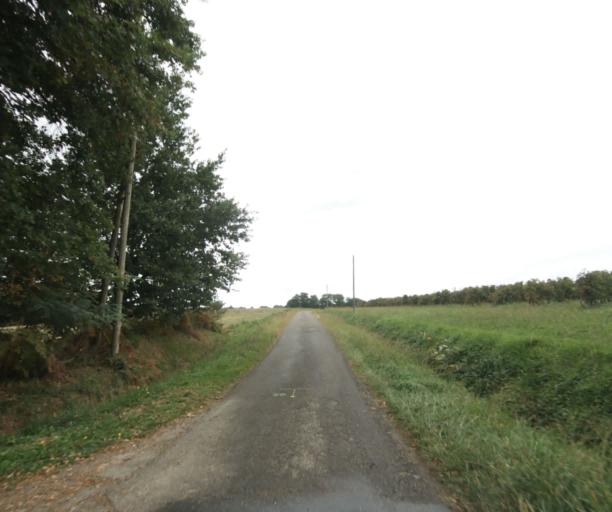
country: FR
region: Midi-Pyrenees
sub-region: Departement du Gers
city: Eauze
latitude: 43.8827
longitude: 0.0703
